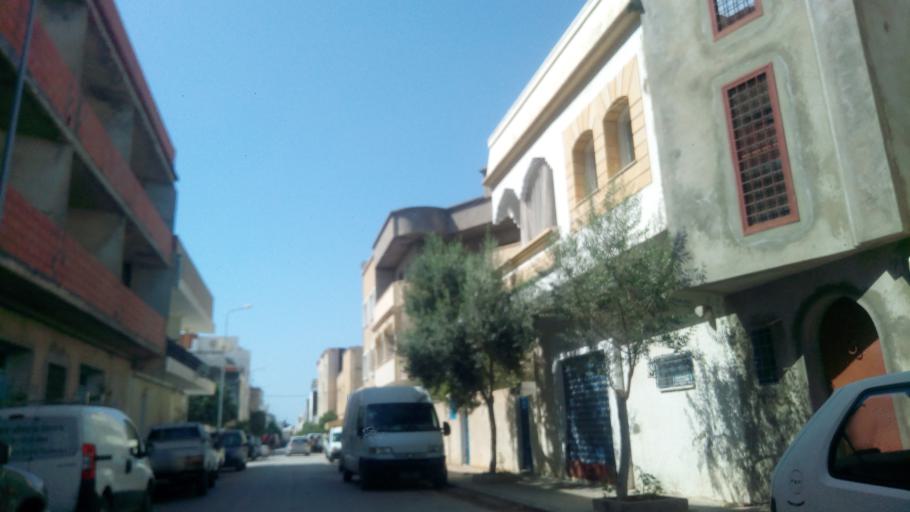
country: TN
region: Nabul
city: Dar Chabanne
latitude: 36.4690
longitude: 10.7454
